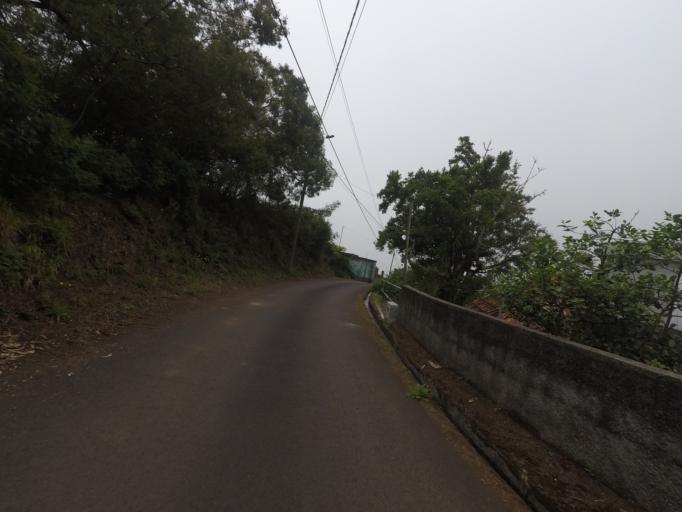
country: PT
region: Madeira
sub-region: Santana
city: Santana
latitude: 32.7488
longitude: -16.8783
